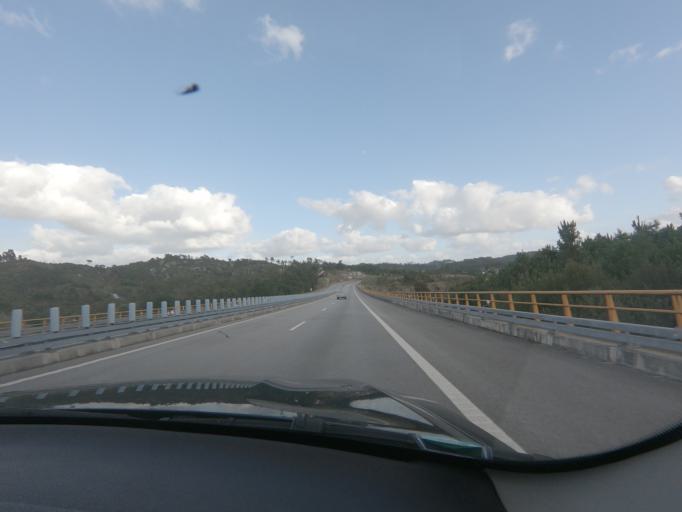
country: PT
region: Viseu
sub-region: Viseu
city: Viseu
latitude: 40.6423
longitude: -7.9619
